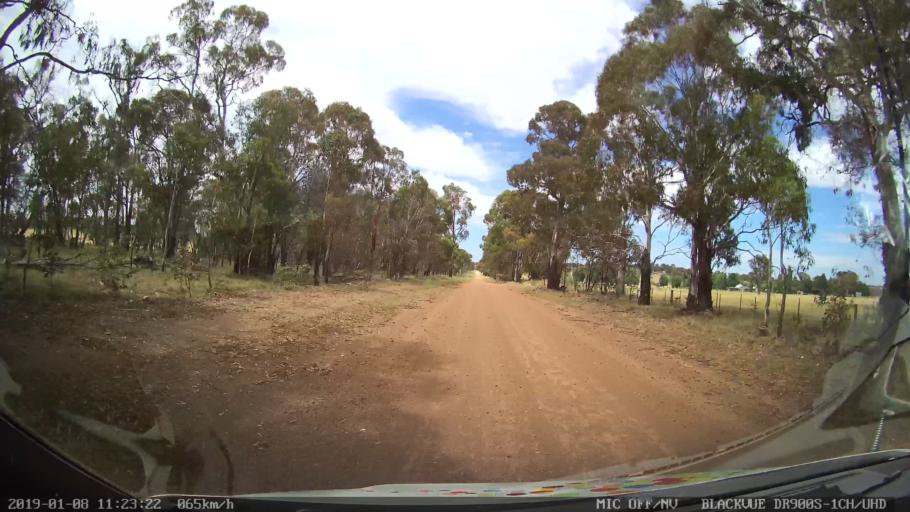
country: AU
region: New South Wales
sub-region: Guyra
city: Guyra
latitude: -30.2546
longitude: 151.5590
